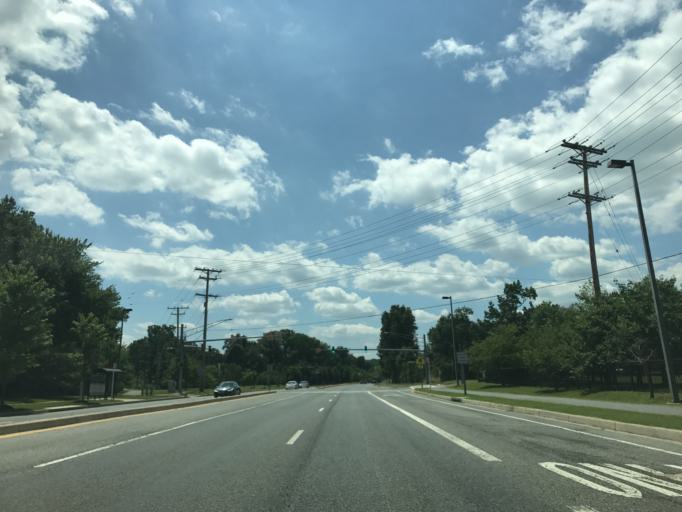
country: US
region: Maryland
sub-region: Prince George's County
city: Bowie
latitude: 38.9753
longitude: -76.7493
